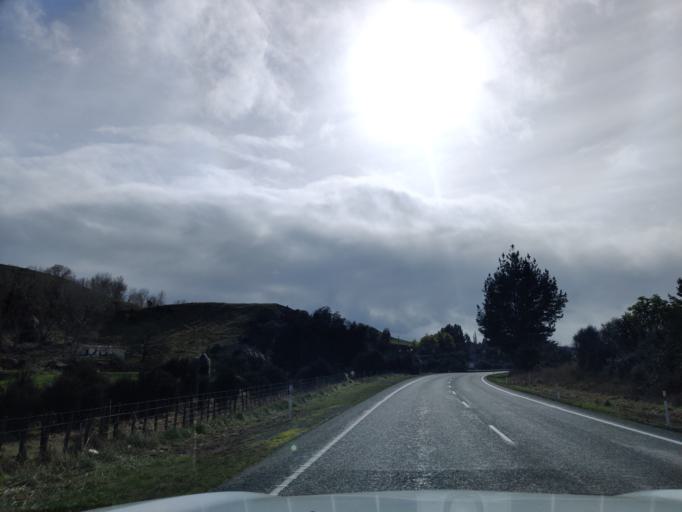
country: NZ
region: Manawatu-Wanganui
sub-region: Ruapehu District
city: Waiouru
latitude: -39.7559
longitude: 175.8296
